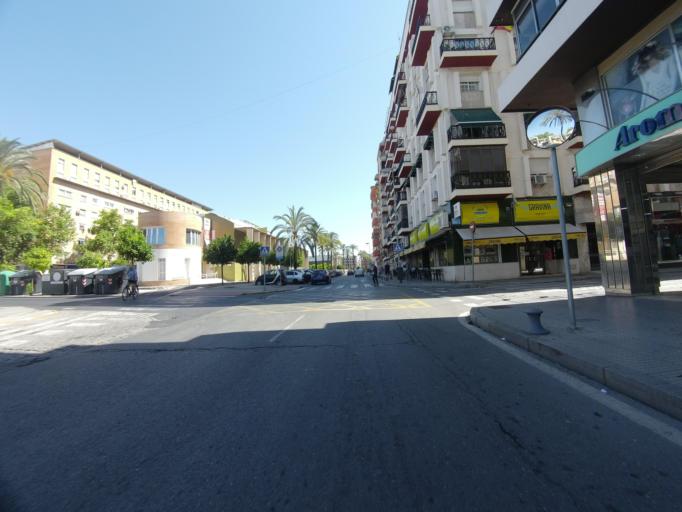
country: ES
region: Andalusia
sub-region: Provincia de Huelva
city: Huelva
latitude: 37.2578
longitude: -6.9563
